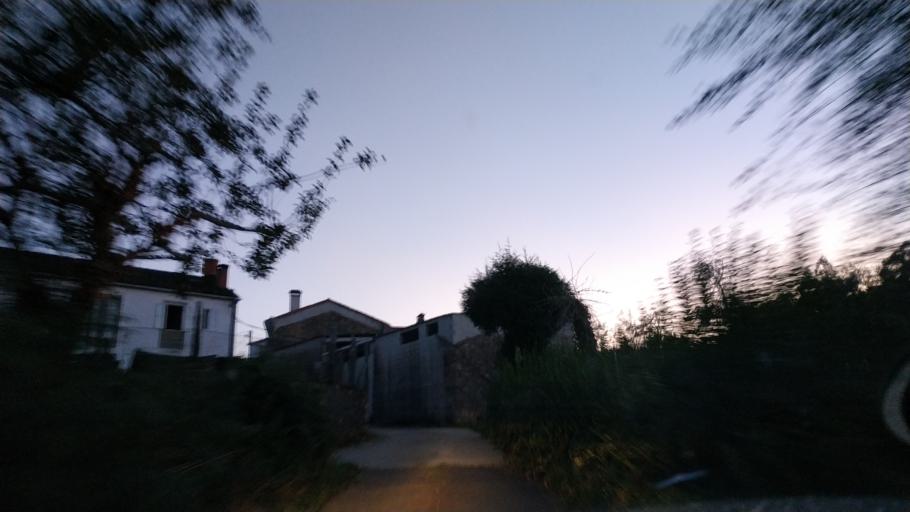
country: ES
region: Galicia
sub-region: Provincia da Coruna
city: Negreira
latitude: 42.9131
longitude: -8.7645
